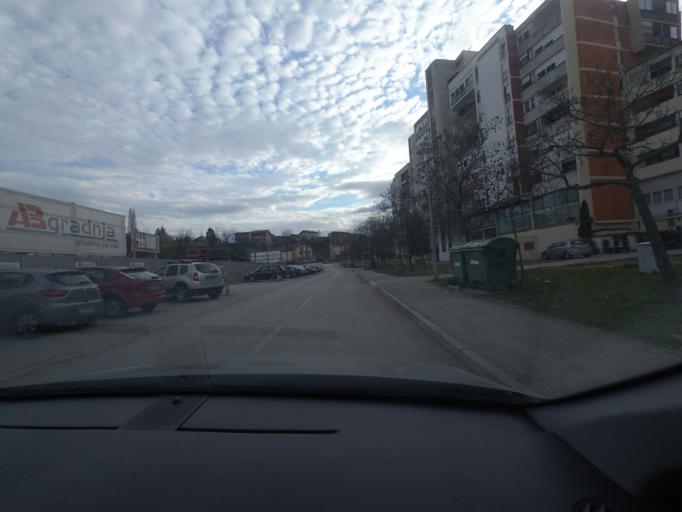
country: HR
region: Karlovacka
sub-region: Grad Karlovac
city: Karlovac
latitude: 45.4809
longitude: 15.5501
